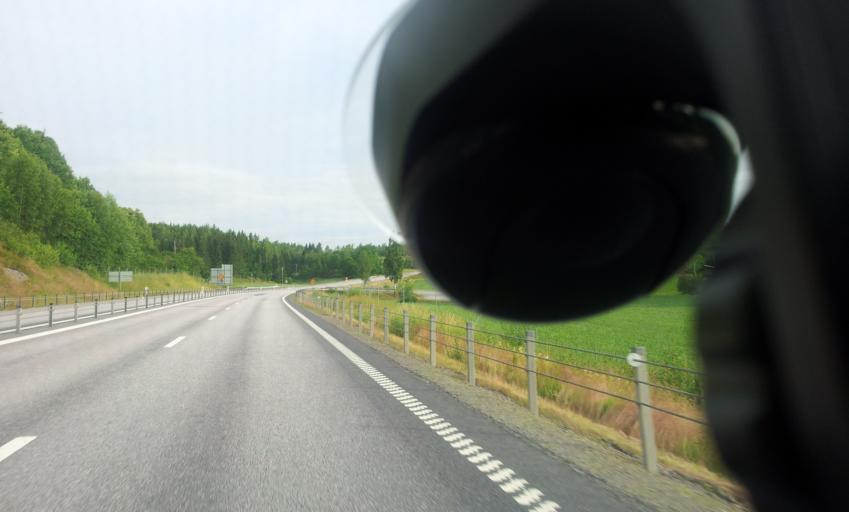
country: SE
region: OEstergoetland
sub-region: Valdemarsviks Kommun
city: Gusum
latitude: 58.2868
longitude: 16.5007
